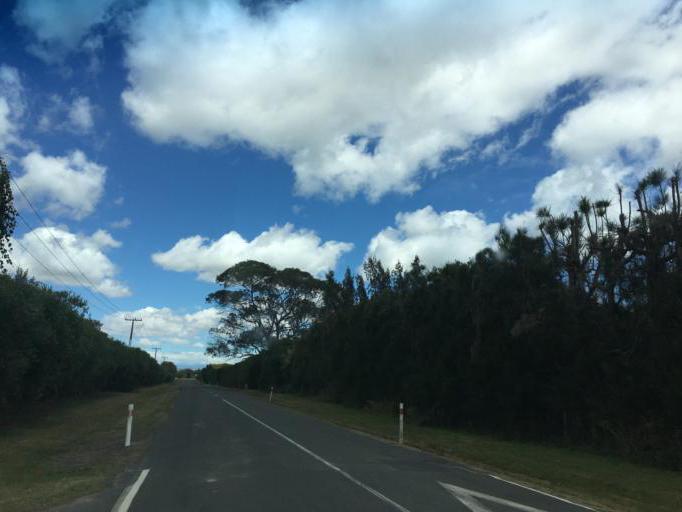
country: NZ
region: Hawke's Bay
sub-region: Hastings District
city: Hastings
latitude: -39.6437
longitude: 176.9084
